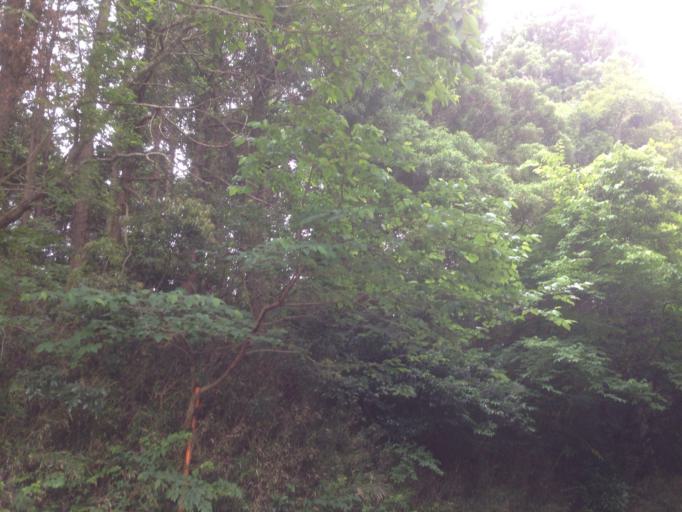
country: JP
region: Chiba
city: Sawara
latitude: 35.7926
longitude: 140.5131
